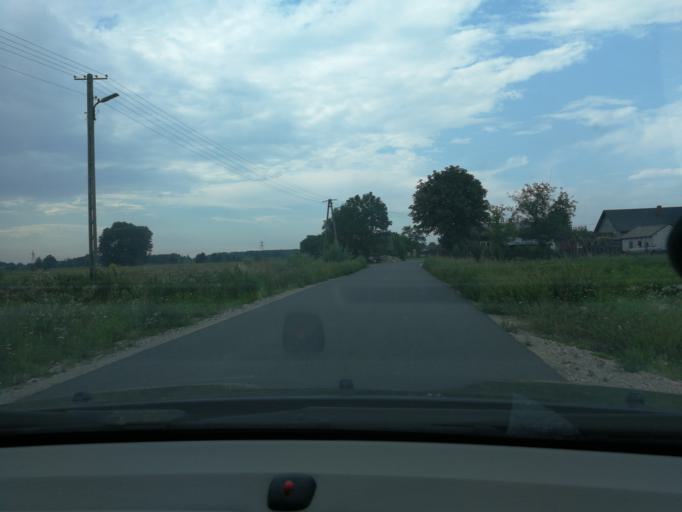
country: PL
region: Masovian Voivodeship
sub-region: Powiat warszawski zachodni
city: Bieniewice
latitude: 52.1053
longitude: 20.5553
